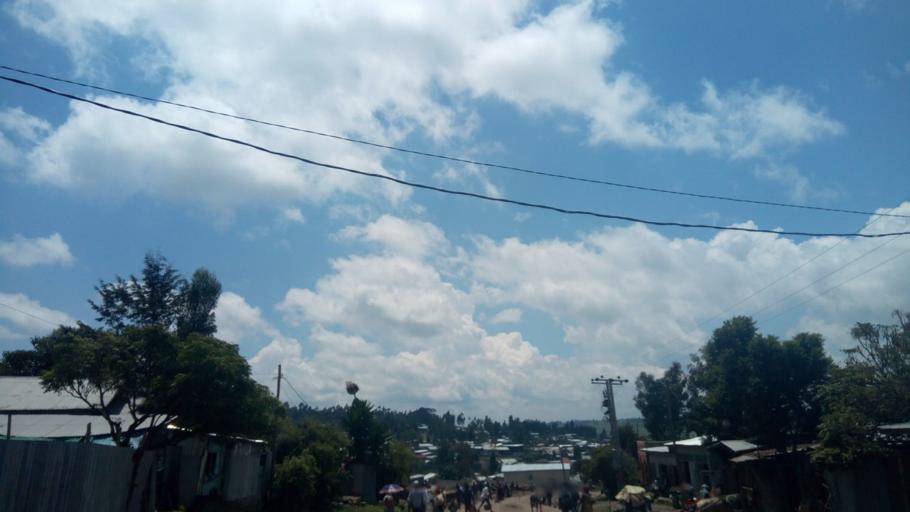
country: ET
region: Oromiya
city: Sendafa
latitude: 8.9705
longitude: 39.1212
